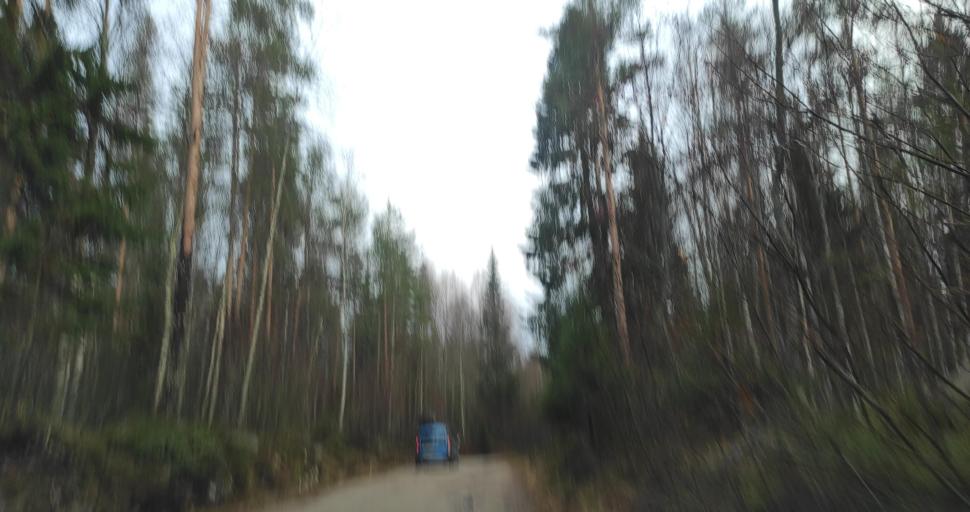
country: RU
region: Republic of Karelia
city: Pitkyaranta
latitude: 61.7378
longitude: 31.3892
